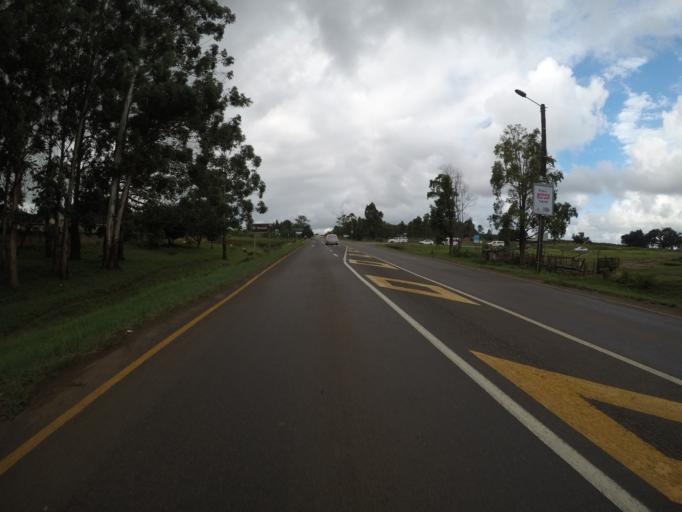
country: ZA
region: KwaZulu-Natal
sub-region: uMkhanyakude District Municipality
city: Mtubatuba
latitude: -28.4104
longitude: 32.1841
